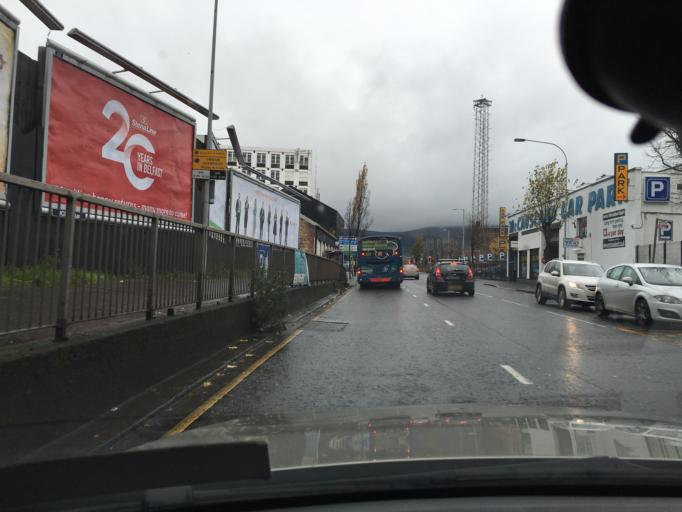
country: GB
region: Northern Ireland
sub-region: City of Belfast
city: Belfast
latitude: 54.5957
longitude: -5.9360
